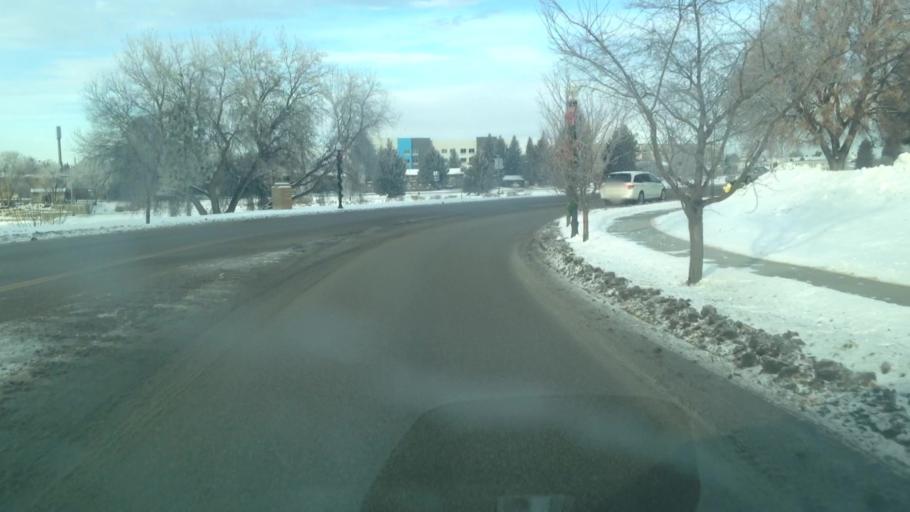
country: US
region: Idaho
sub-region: Bonneville County
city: Idaho Falls
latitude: 43.4975
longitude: -112.0411
